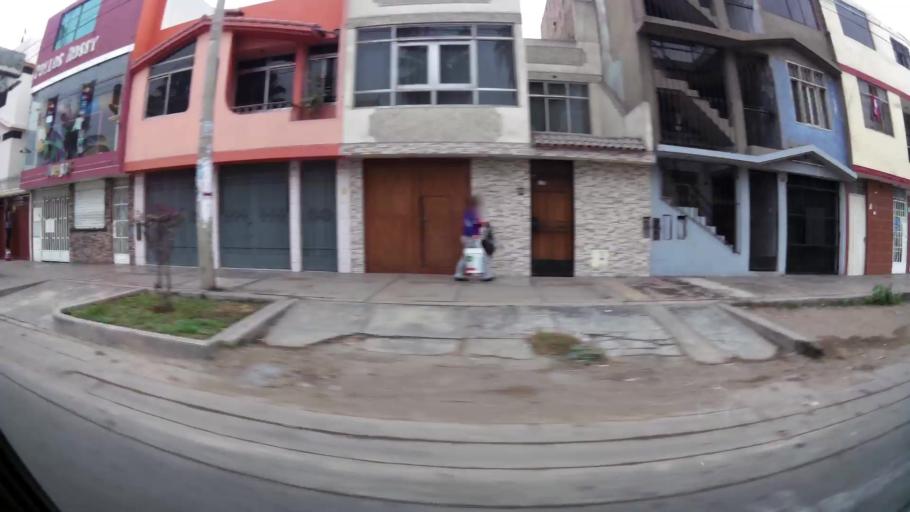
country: PE
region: Lima
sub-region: Lima
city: Independencia
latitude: -11.9677
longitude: -77.0712
